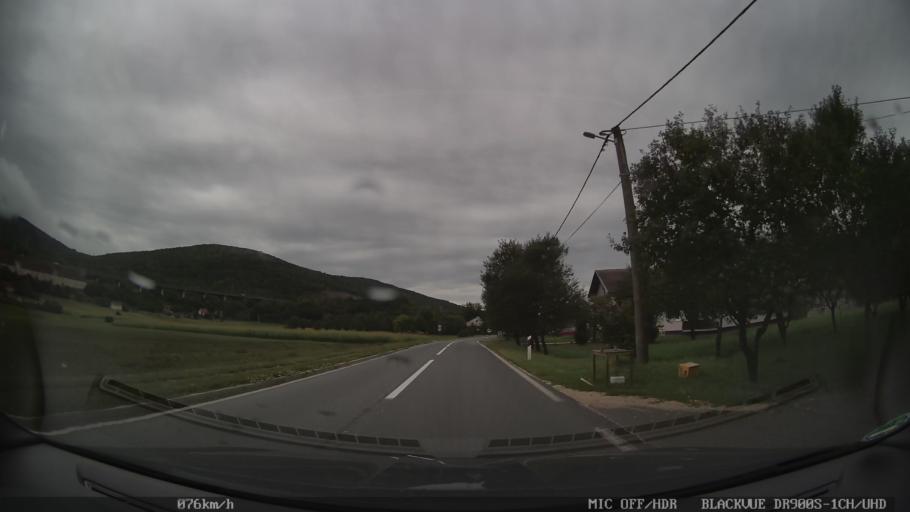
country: HR
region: Licko-Senjska
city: Otocac
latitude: 44.9080
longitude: 15.1692
